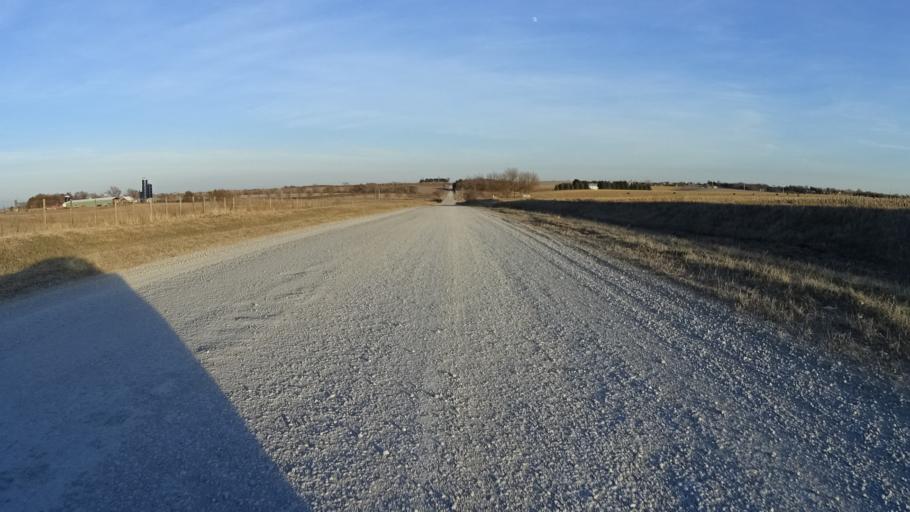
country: US
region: Nebraska
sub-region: Sarpy County
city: Springfield
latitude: 41.1326
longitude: -96.1268
